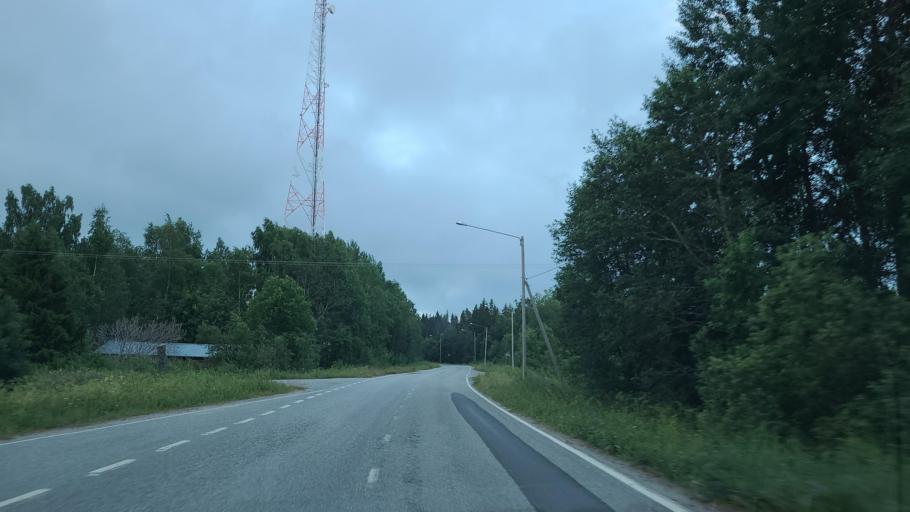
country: FI
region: Ostrobothnia
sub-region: Vaasa
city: Replot
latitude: 63.2875
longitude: 21.1161
